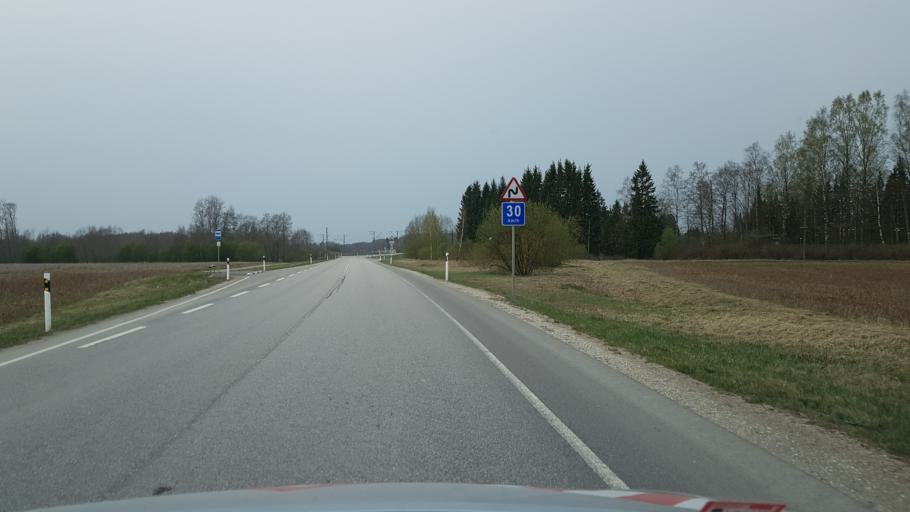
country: EE
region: Harju
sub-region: Raasiku vald
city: Arukula
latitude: 59.3819
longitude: 25.0044
